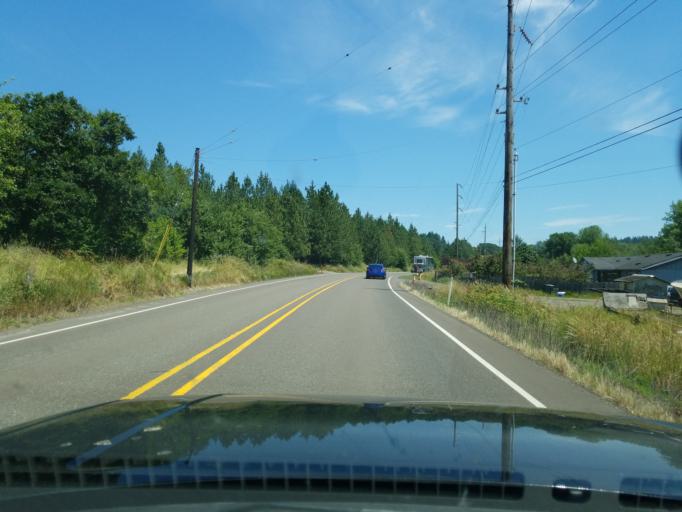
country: US
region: Oregon
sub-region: Yamhill County
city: Yamhill
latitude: 45.3716
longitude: -123.1601
